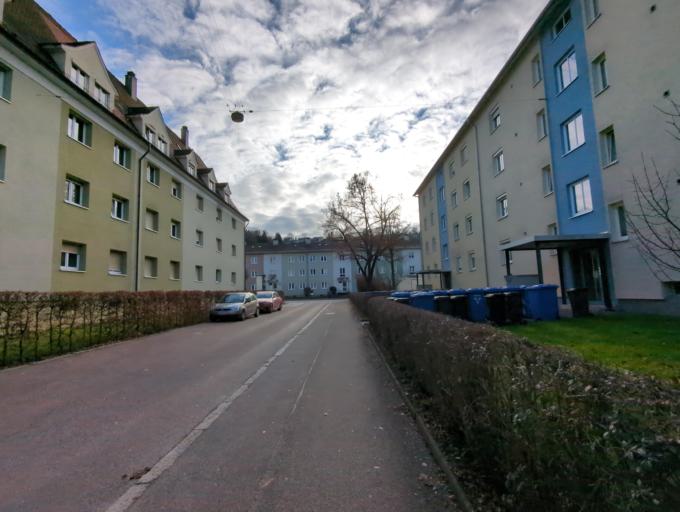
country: DE
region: Baden-Wuerttemberg
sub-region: Regierungsbezirk Stuttgart
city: Schwabisch Gmund
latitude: 48.8020
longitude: 9.8111
